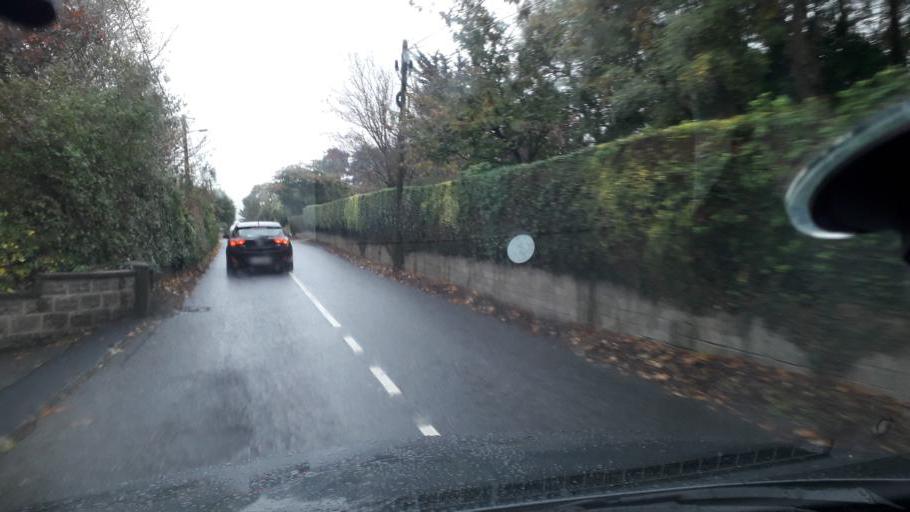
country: IE
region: Leinster
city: Ballyboden
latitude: 53.2643
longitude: -6.3126
